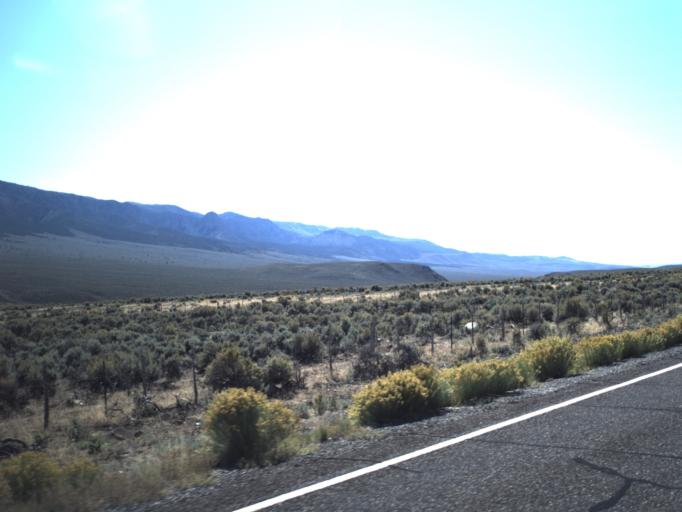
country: US
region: Utah
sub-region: Piute County
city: Junction
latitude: 38.3357
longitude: -111.9553
